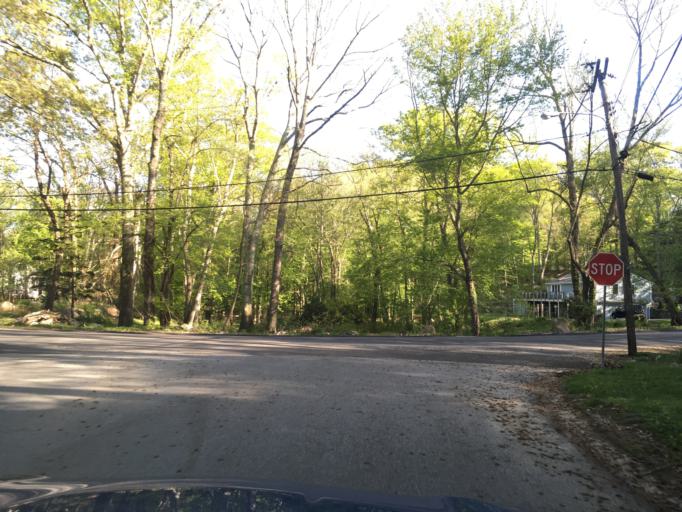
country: US
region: Rhode Island
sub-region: Washington County
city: Exeter
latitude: 41.6081
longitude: -71.5160
